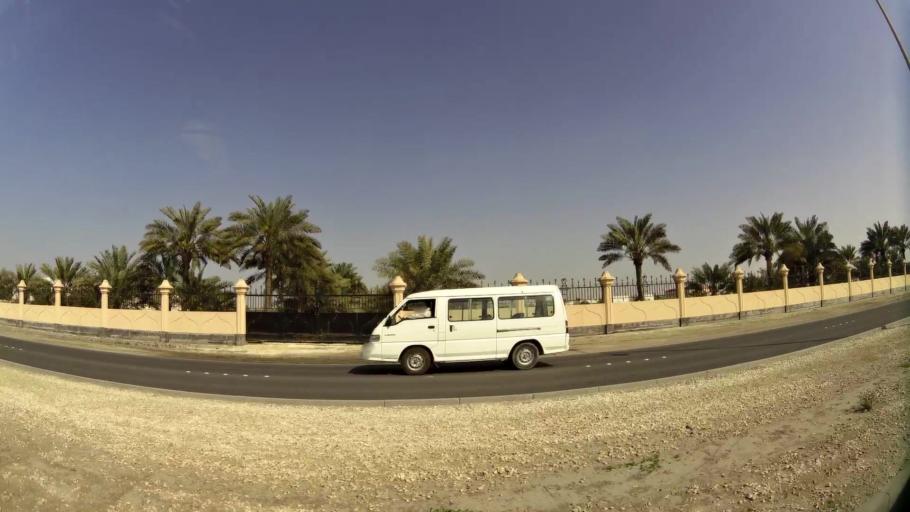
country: BH
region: Central Governorate
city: Madinat Hamad
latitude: 26.1771
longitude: 50.4655
